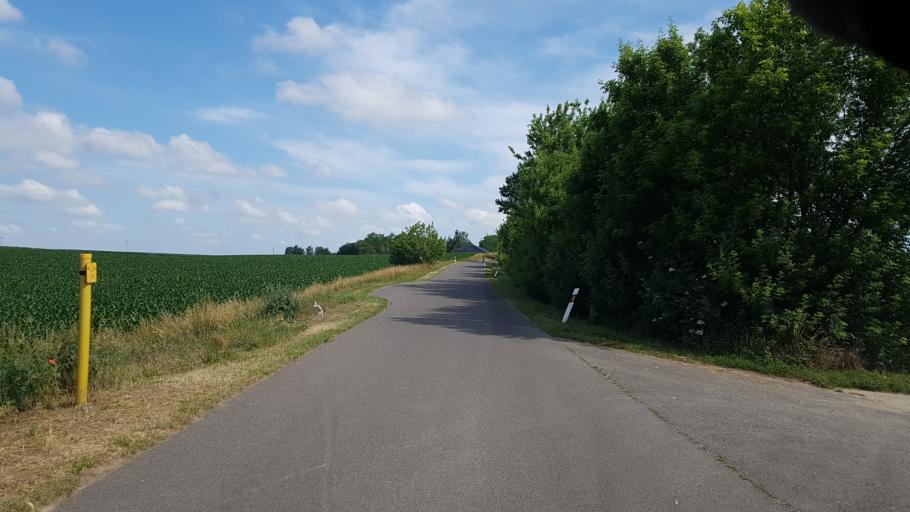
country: DE
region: Brandenburg
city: Prenzlau
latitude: 53.3779
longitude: 13.8045
